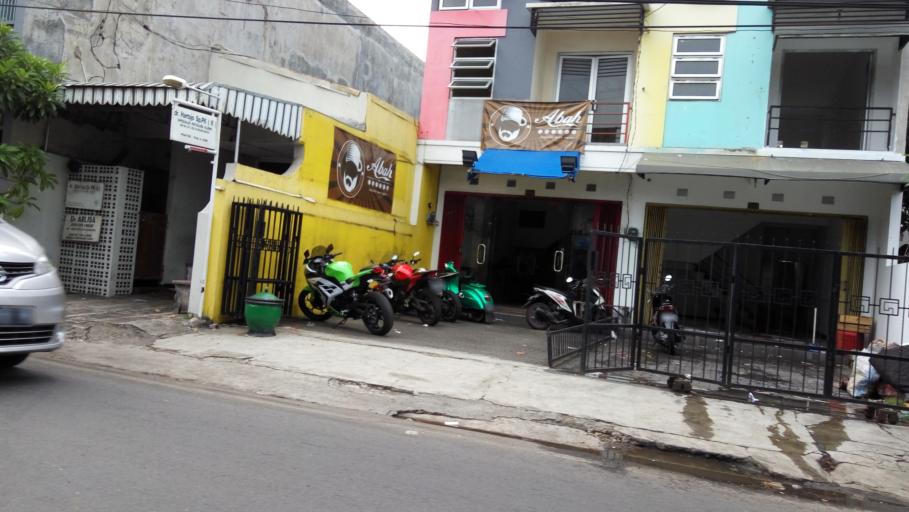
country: ID
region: East Java
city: Malang
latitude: -7.9443
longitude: 112.6099
